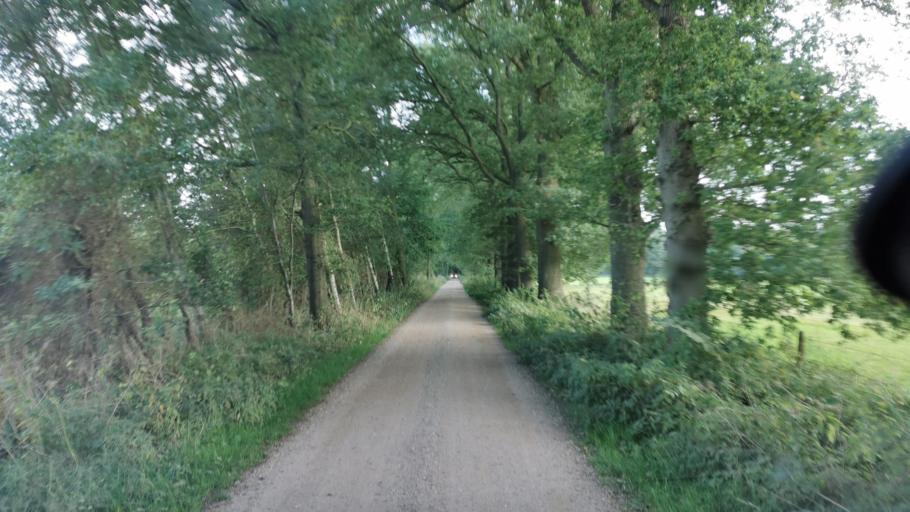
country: NL
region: Overijssel
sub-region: Gemeente Oldenzaal
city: Oldenzaal
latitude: 52.2979
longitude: 6.9736
